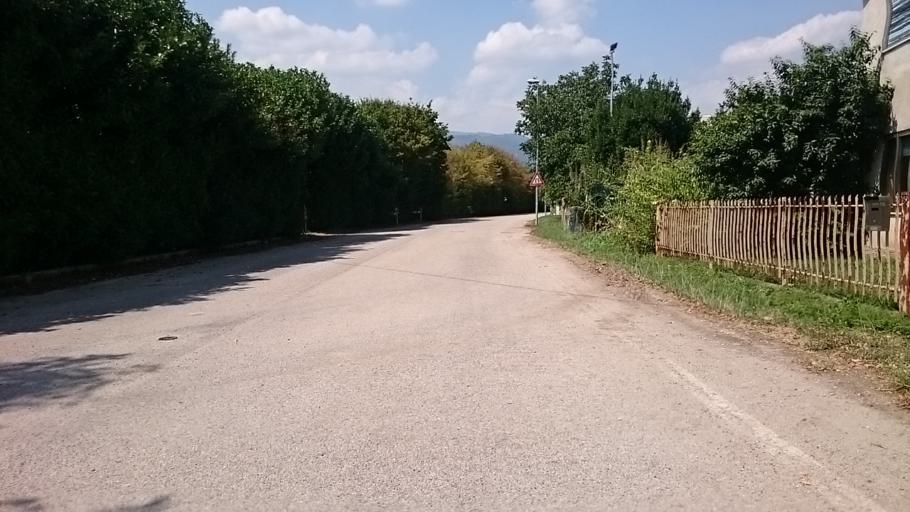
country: IT
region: Veneto
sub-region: Provincia di Vicenza
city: Bassano del Grappa
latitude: 45.7403
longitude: 11.7239
